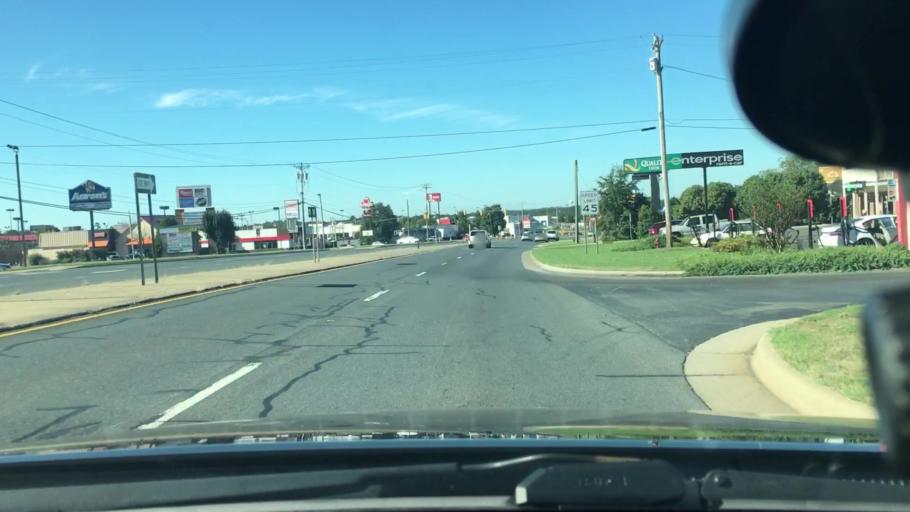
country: US
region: North Carolina
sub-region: Stanly County
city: Albemarle
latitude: 35.3454
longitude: -80.1700
